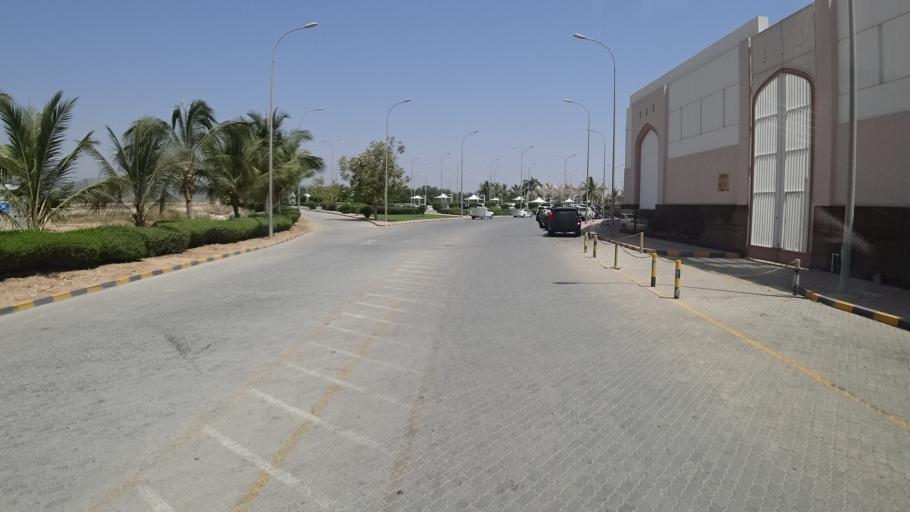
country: OM
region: Zufar
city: Salalah
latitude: 17.0237
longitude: 54.0643
